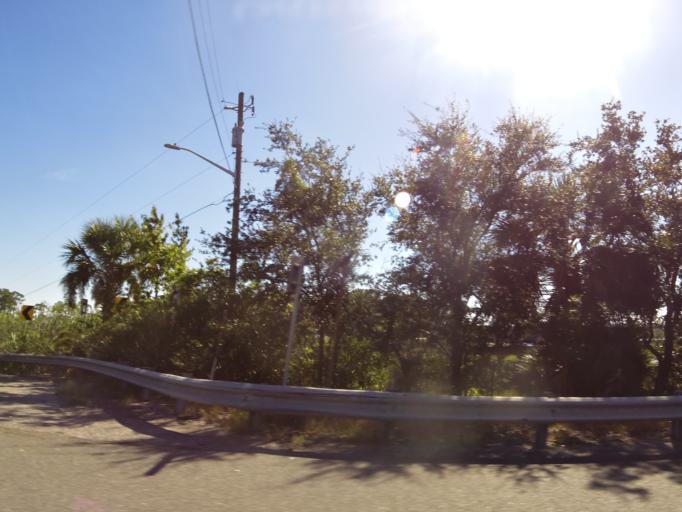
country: US
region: Florida
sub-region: Duval County
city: Jacksonville
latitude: 30.4119
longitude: -81.5504
